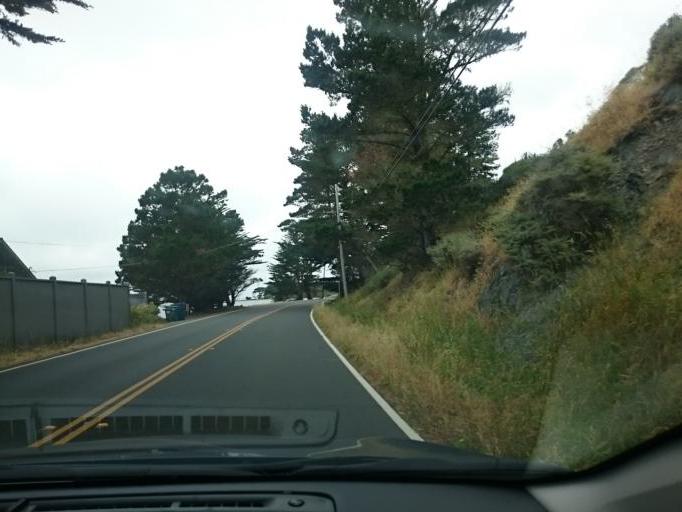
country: US
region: California
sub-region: Marin County
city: Inverness
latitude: 38.1585
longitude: -122.8939
